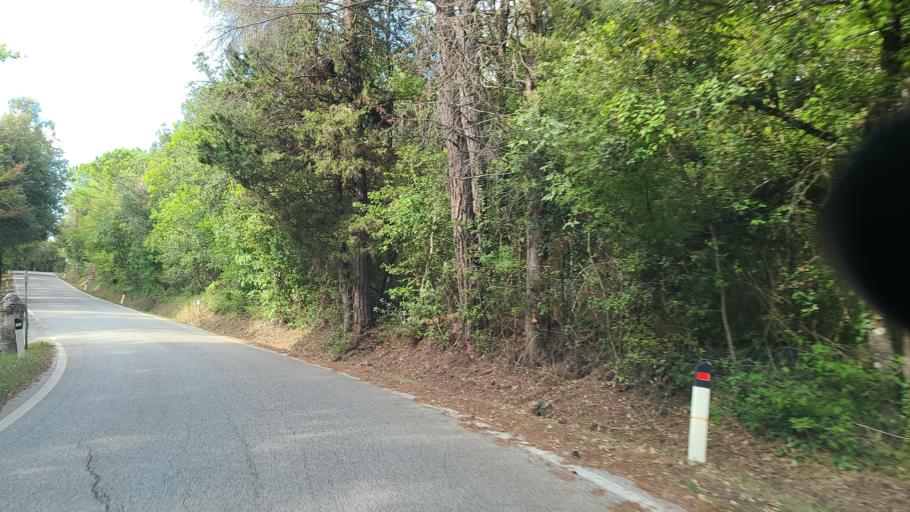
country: IT
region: Tuscany
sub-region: Provincia di Siena
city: San Gimignano
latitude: 43.4187
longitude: 10.9764
